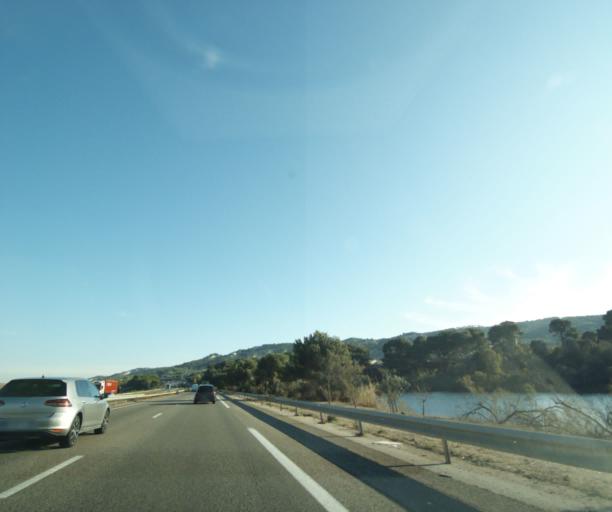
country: FR
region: Provence-Alpes-Cote d'Azur
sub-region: Departement des Bouches-du-Rhone
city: Chateauneuf-les-Martigues
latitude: 43.3995
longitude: 5.1193
